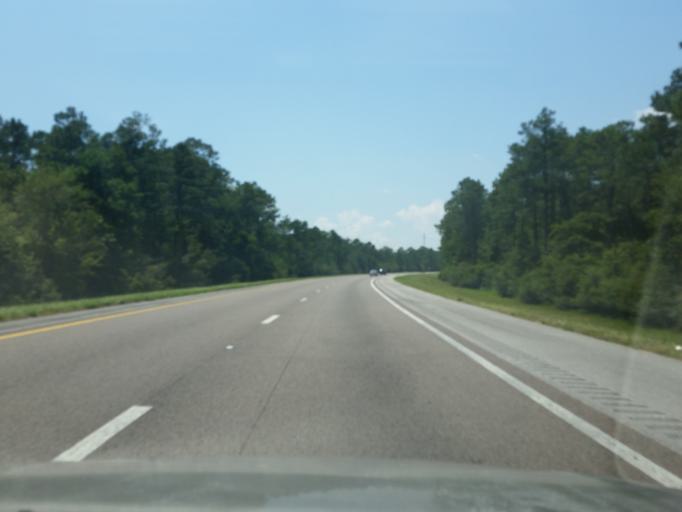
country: US
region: Florida
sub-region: Escambia County
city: Cantonment
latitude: 30.5812
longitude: -87.5124
